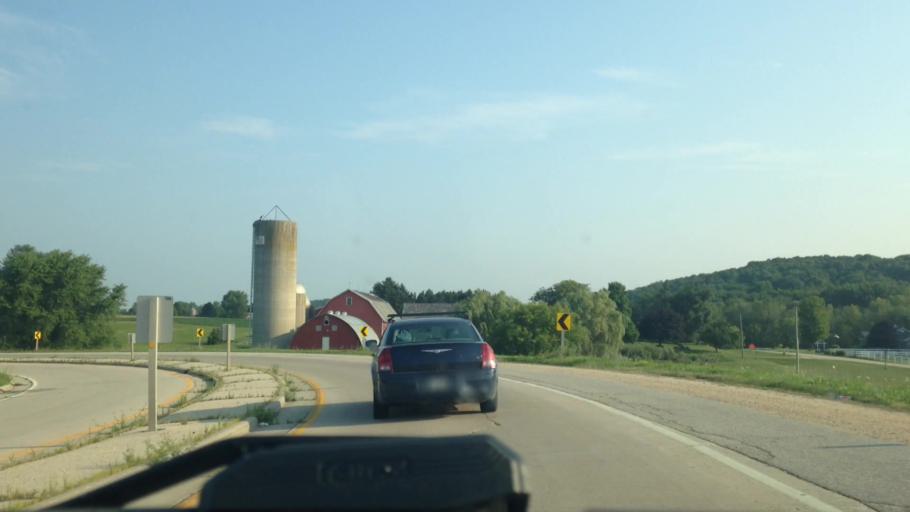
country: US
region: Wisconsin
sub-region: Dodge County
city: Theresa
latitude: 43.5379
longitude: -88.4010
